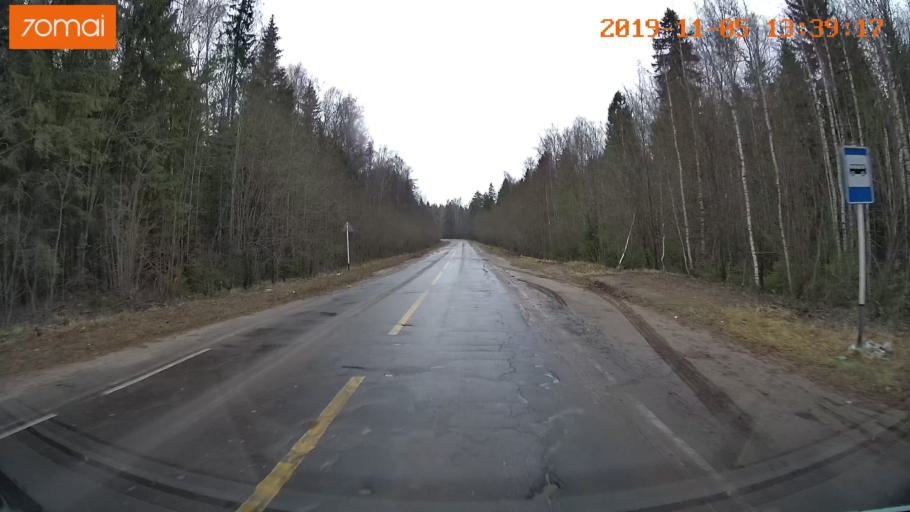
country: RU
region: Ivanovo
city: Shuya
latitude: 56.9383
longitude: 41.3868
